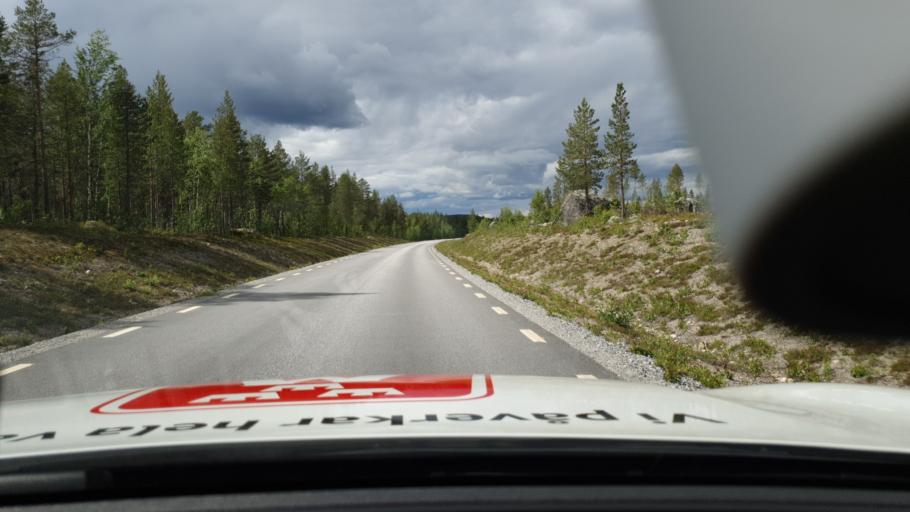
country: SE
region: Norrbotten
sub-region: Jokkmokks Kommun
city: Jokkmokk
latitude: 66.8192
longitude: 19.1582
